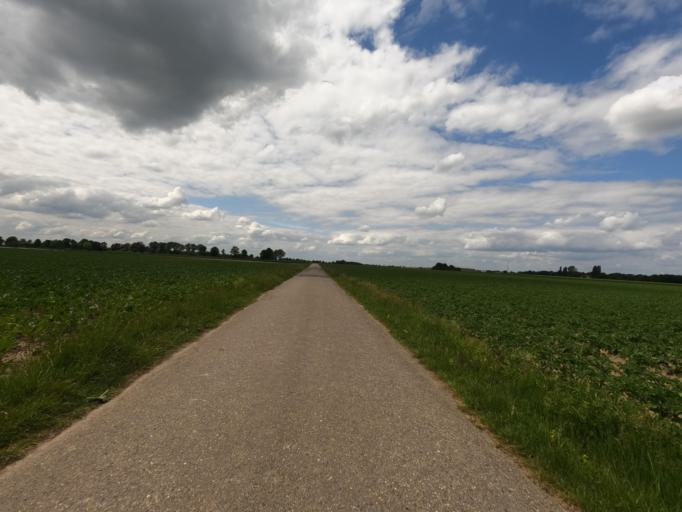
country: DE
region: North Rhine-Westphalia
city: Geilenkirchen
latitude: 50.9615
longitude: 6.1006
